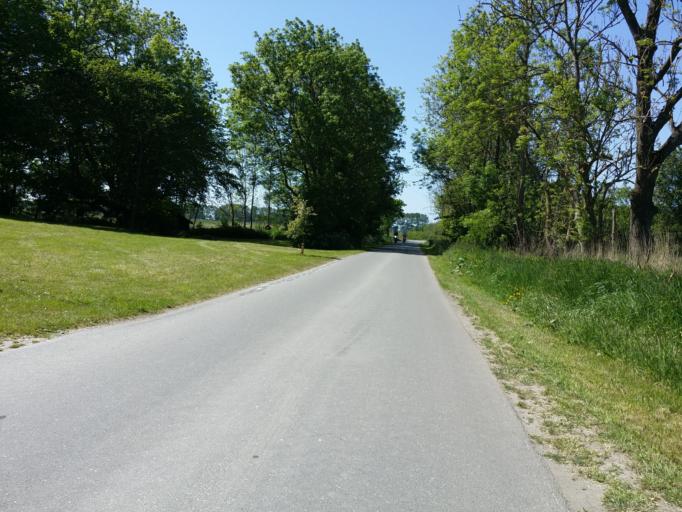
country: DE
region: Lower Saxony
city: Stedesdorf
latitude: 53.6726
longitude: 7.6733
